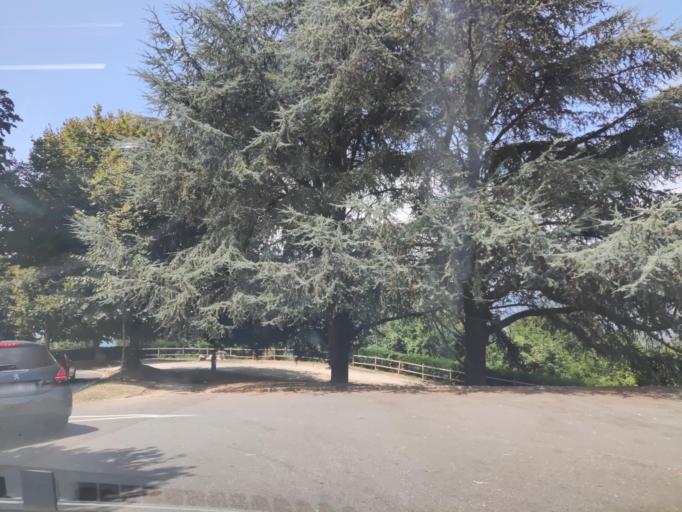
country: ES
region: Galicia
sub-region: Provincia de Pontevedra
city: Vigo
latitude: 42.2569
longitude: -8.7021
